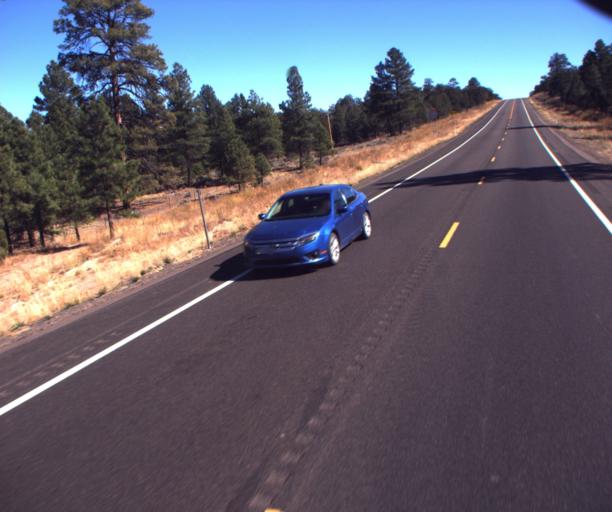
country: US
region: Arizona
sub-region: Apache County
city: Ganado
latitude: 35.7076
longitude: -109.3162
